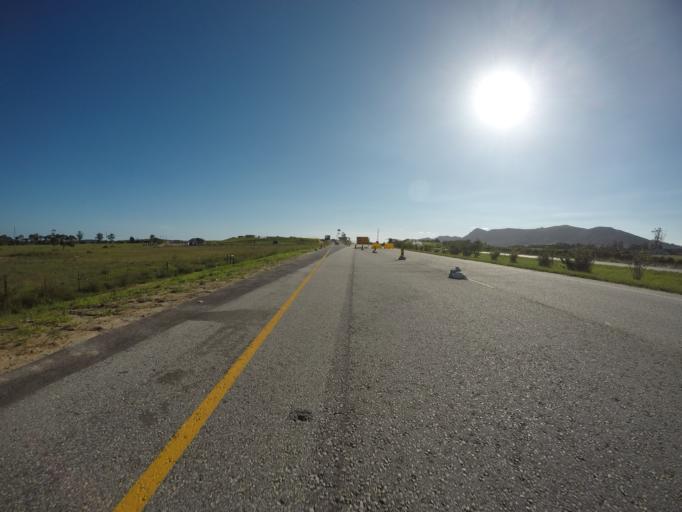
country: ZA
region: Eastern Cape
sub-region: Nelson Mandela Bay Metropolitan Municipality
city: Uitenhage
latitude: -33.9201
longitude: 25.2971
